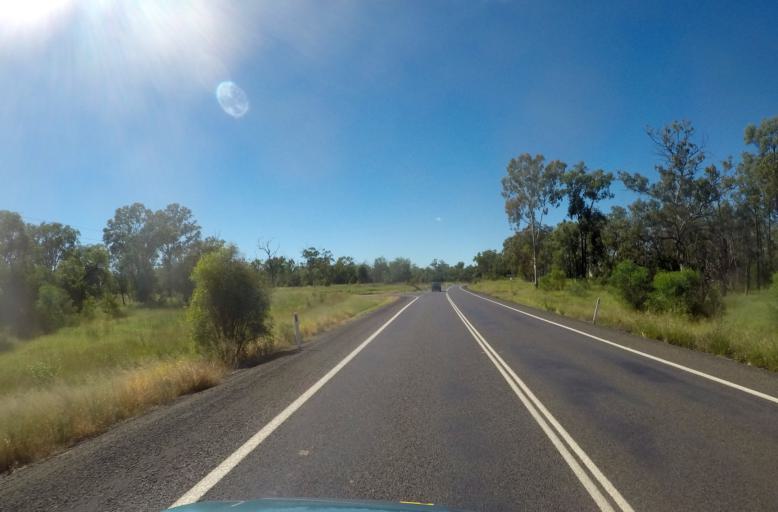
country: AU
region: Queensland
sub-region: Maranoa
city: Roma
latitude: -26.5805
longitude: 148.9614
